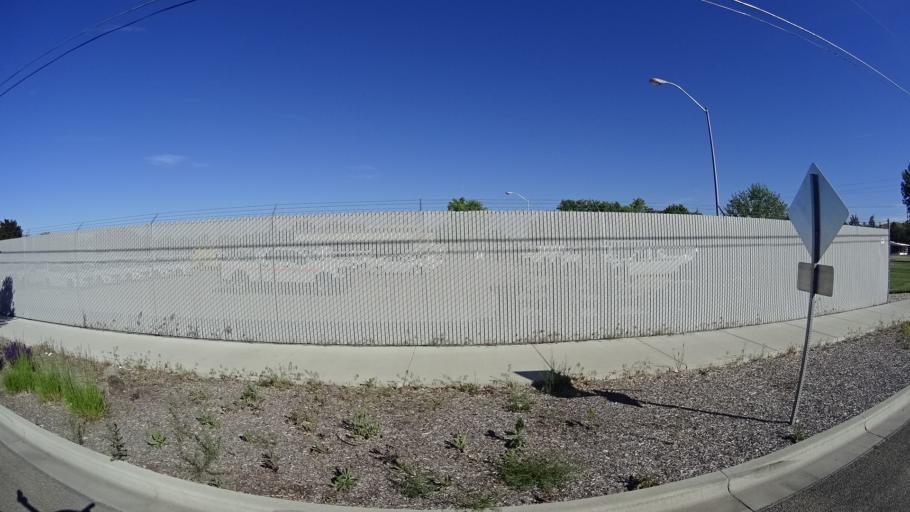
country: US
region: Idaho
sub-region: Ada County
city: Garden City
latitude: 43.6340
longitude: -116.2283
